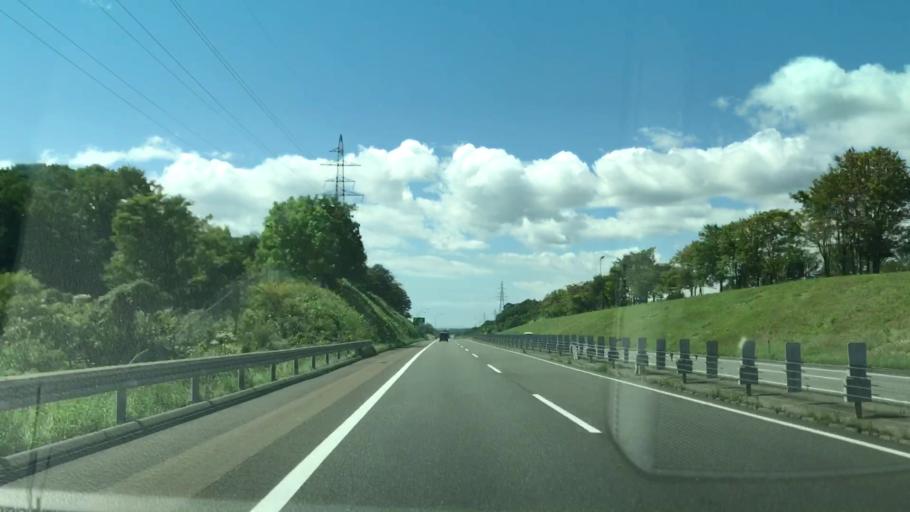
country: JP
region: Hokkaido
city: Tomakomai
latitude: 42.6154
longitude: 141.4703
